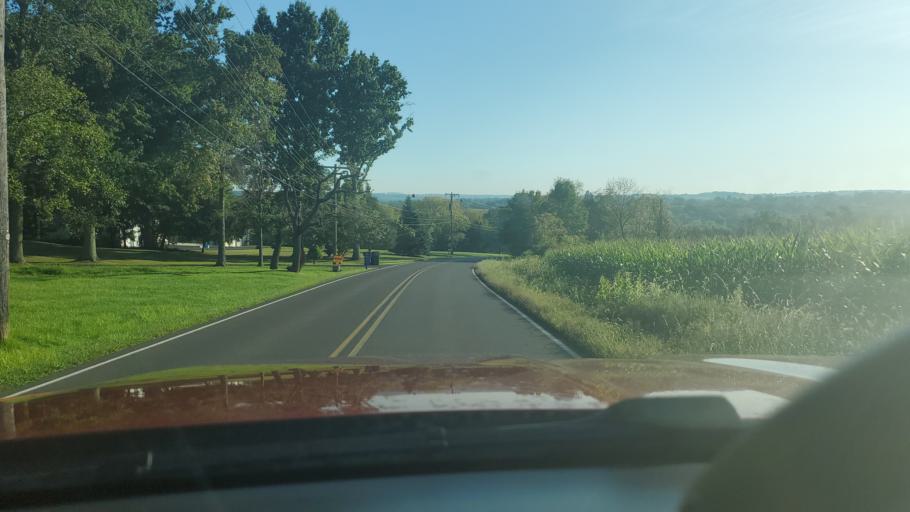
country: US
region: Pennsylvania
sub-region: Montgomery County
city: Woxall
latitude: 40.2923
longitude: -75.4250
